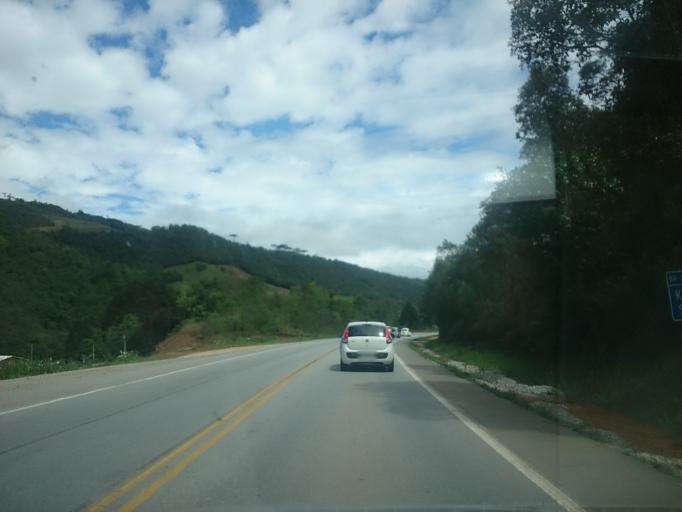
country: BR
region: Santa Catarina
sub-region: Anitapolis
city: Anitapolis
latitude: -27.6834
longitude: -49.2223
